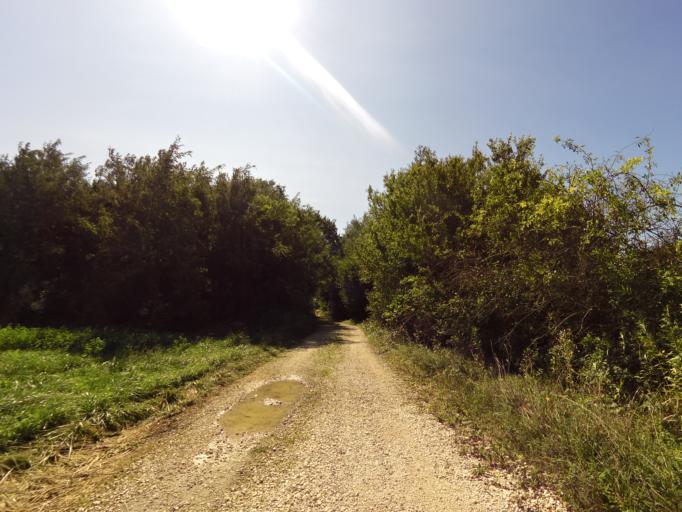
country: HU
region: Veszprem
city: Tapolca
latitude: 46.8358
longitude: 17.3985
